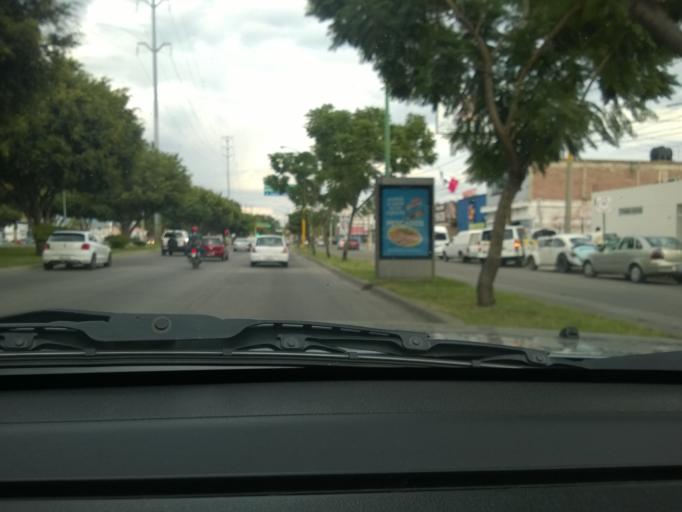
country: MX
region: Guanajuato
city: Leon
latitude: 21.1517
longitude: -101.6721
